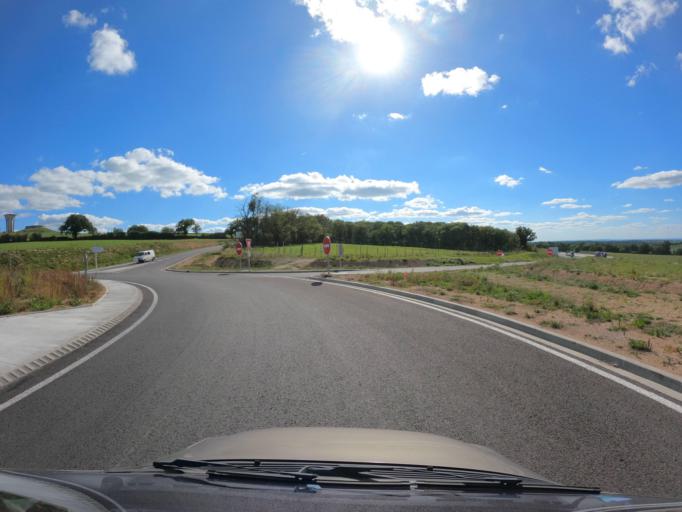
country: FR
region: Auvergne
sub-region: Departement de l'Allier
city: Buxieres-les-Mines
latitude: 46.3986
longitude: 3.0446
